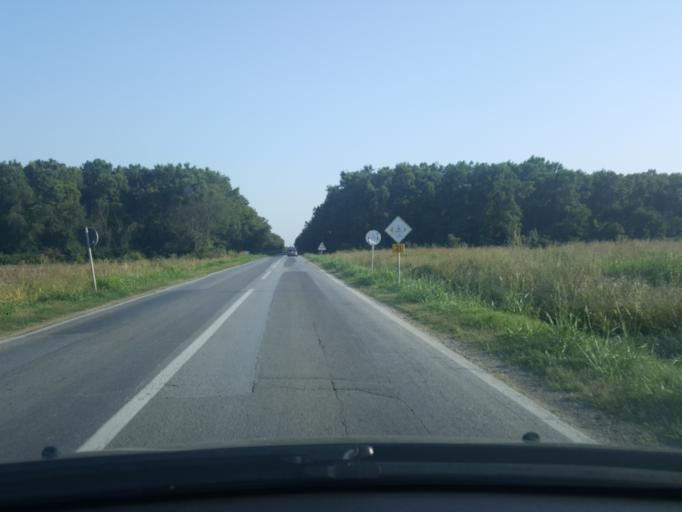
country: RS
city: Jarak
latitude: 44.9055
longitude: 19.7646
